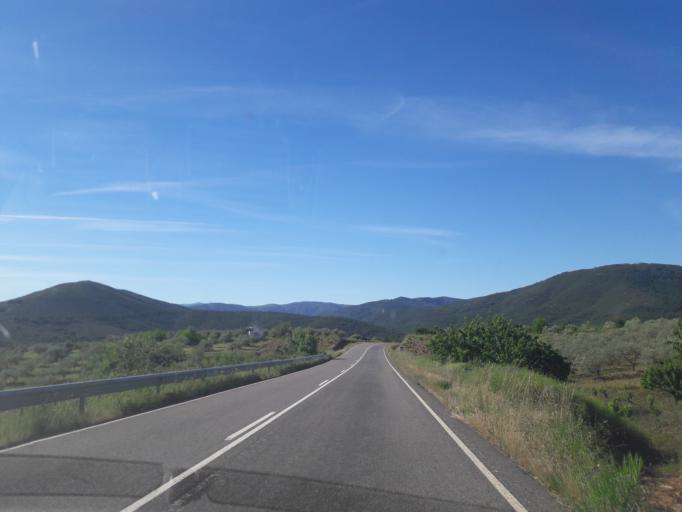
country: ES
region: Castille and Leon
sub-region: Provincia de Salamanca
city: Sotoserrano
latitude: 40.4272
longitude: -6.0329
